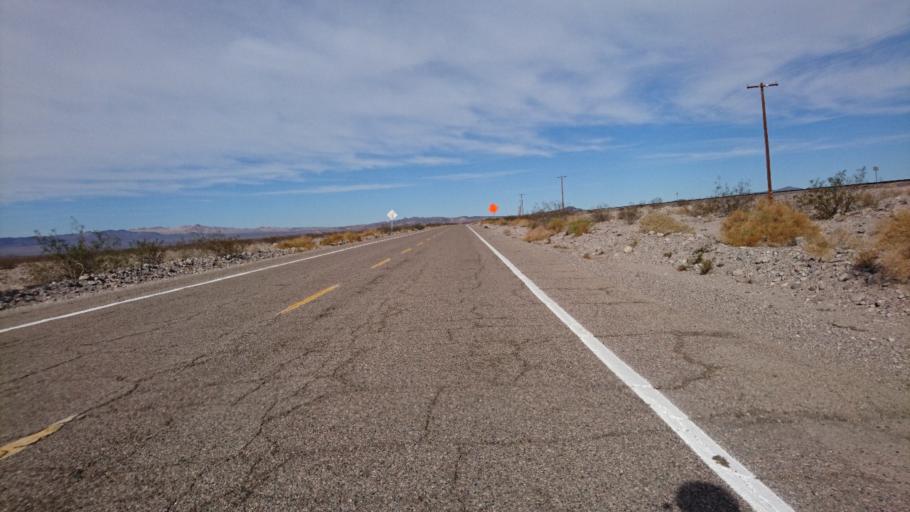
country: US
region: California
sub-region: San Bernardino County
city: Twentynine Palms
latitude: 34.6065
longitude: -115.9633
